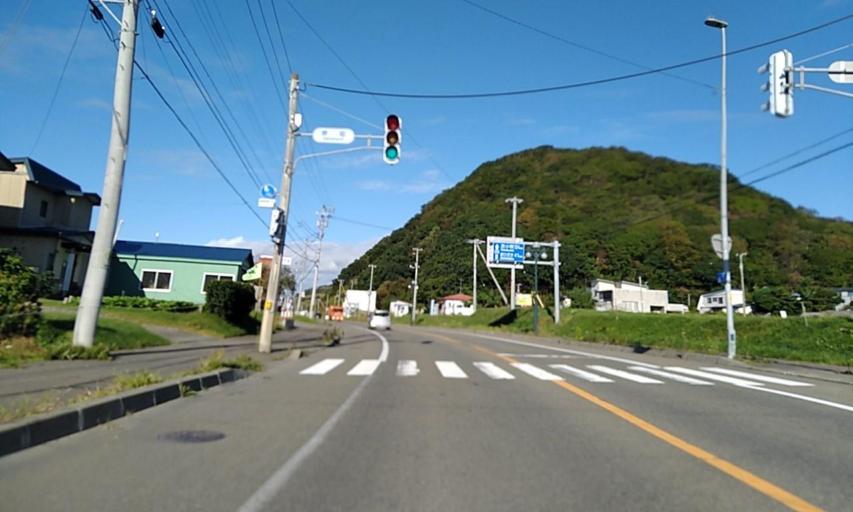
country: JP
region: Hokkaido
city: Shizunai-furukawacho
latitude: 42.1763
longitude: 142.7574
